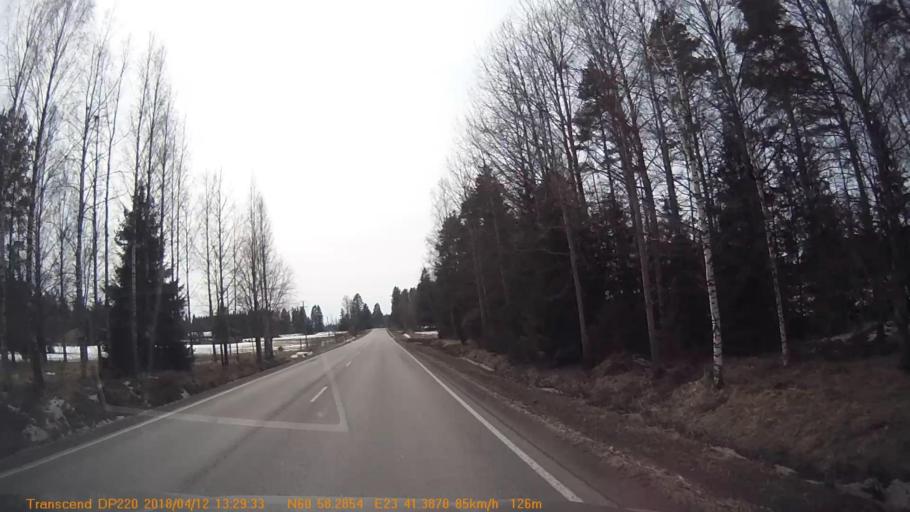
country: FI
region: Haeme
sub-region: Forssa
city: Forssa
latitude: 60.9712
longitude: 23.6894
